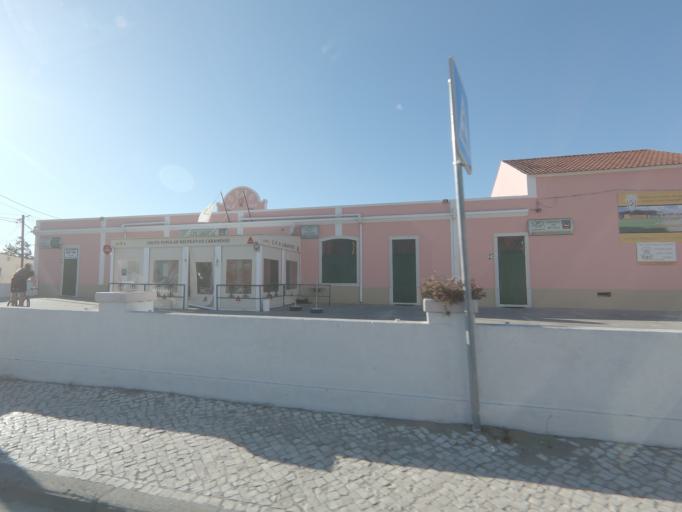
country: PT
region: Setubal
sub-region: Palmela
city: Quinta do Anjo
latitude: 38.5563
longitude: -8.9683
